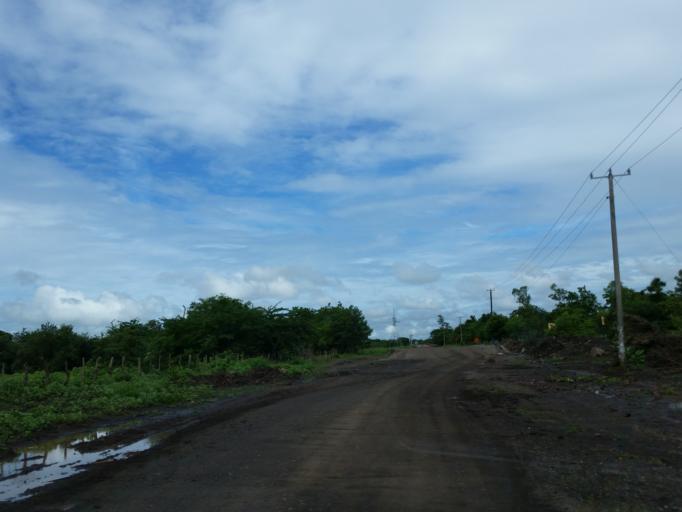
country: NI
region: Leon
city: Larreynaga
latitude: 12.5808
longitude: -86.6284
